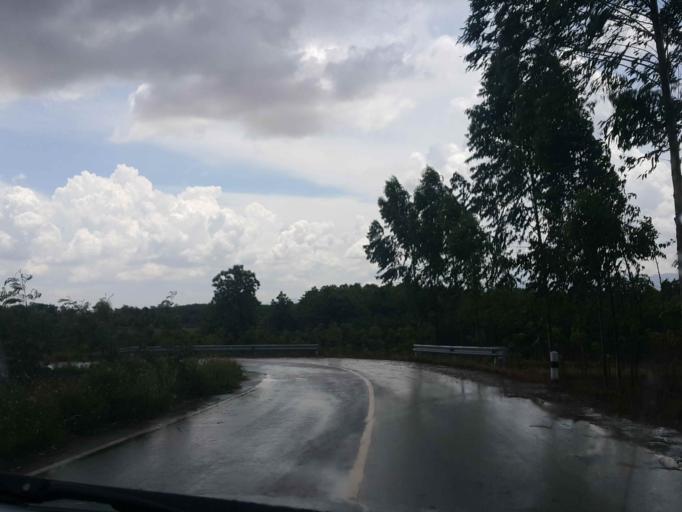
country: TH
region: Phayao
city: Dok Kham Tai
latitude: 19.0380
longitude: 99.9825
